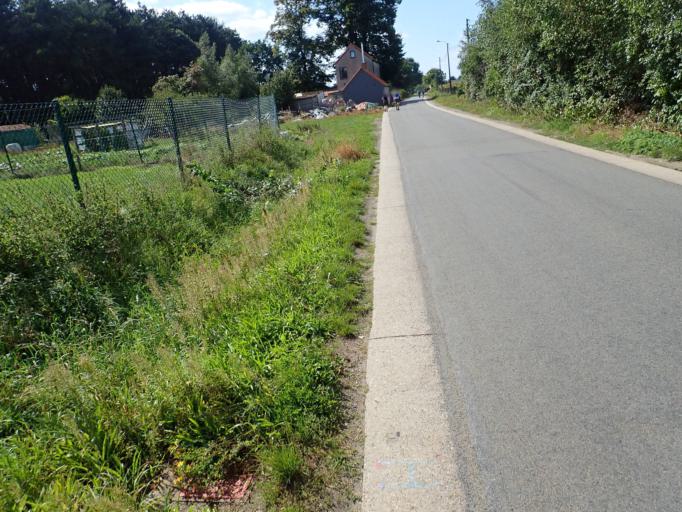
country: BE
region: Flanders
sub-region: Provincie Antwerpen
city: Olen
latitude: 51.1308
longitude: 4.8892
